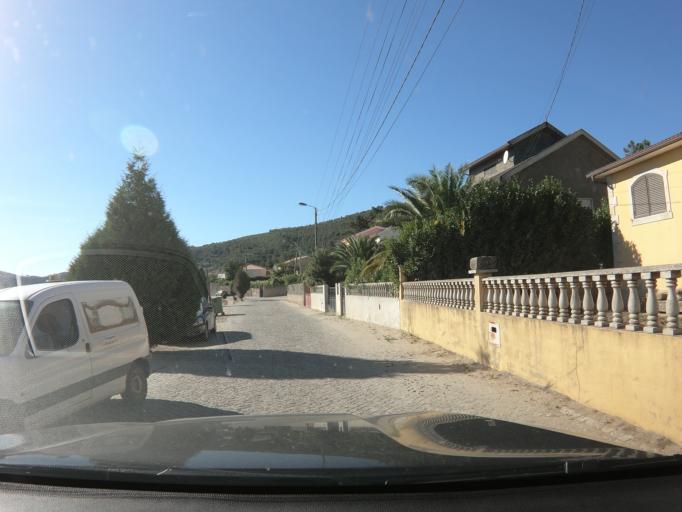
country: PT
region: Vila Real
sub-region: Sabrosa
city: Vilela
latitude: 41.2197
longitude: -7.5666
